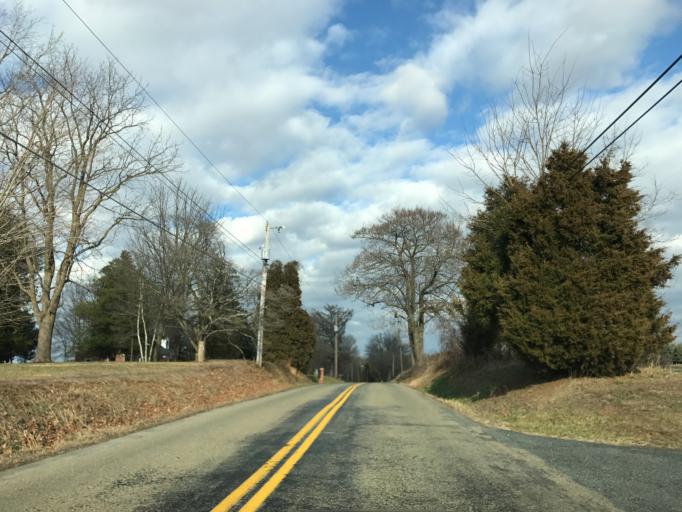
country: US
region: Maryland
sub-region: Harford County
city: Havre de Grace
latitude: 39.6413
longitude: -76.1883
